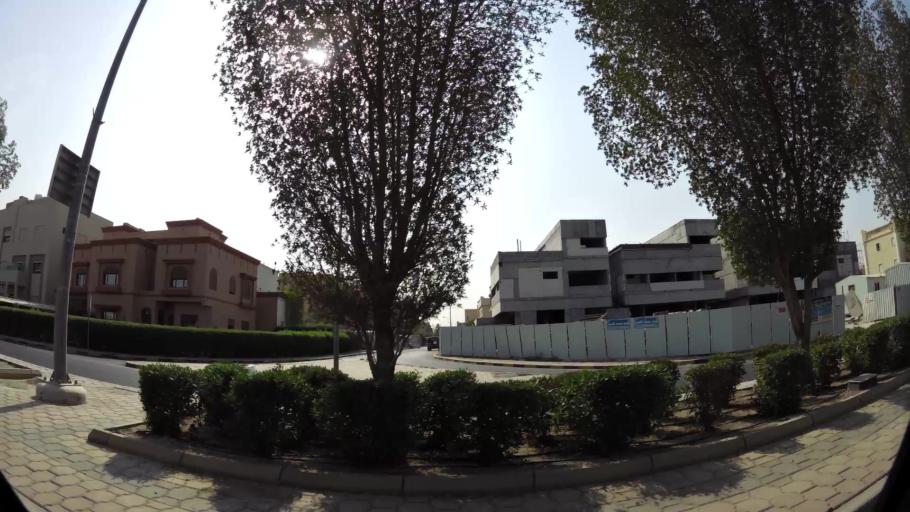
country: KW
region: Mubarak al Kabir
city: Sabah as Salim
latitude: 29.2757
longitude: 48.0445
